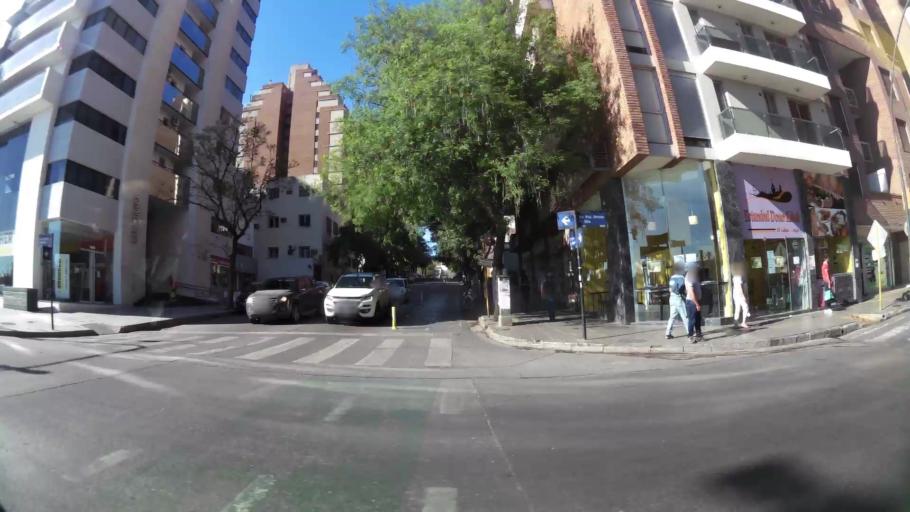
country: AR
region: Cordoba
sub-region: Departamento de Capital
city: Cordoba
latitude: -31.4232
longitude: -64.1768
